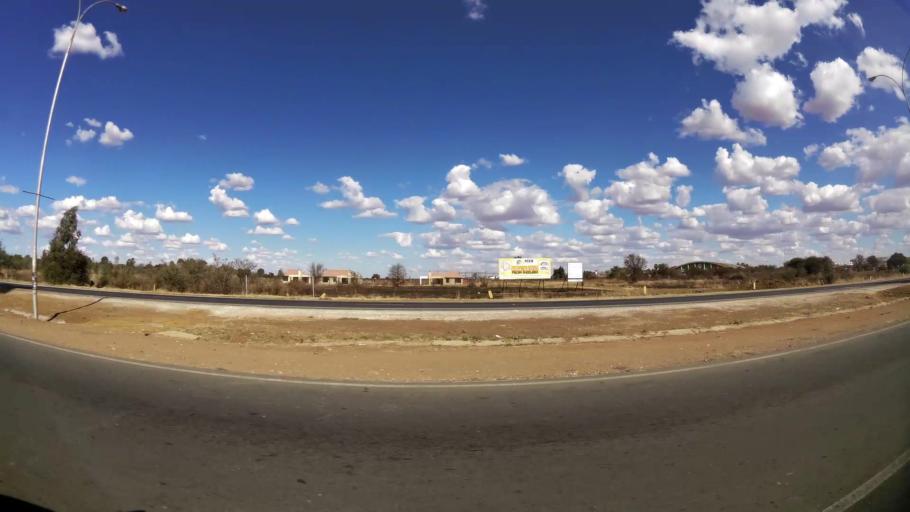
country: ZA
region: North-West
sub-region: Dr Kenneth Kaunda District Municipality
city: Klerksdorp
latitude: -26.8677
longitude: 26.6300
